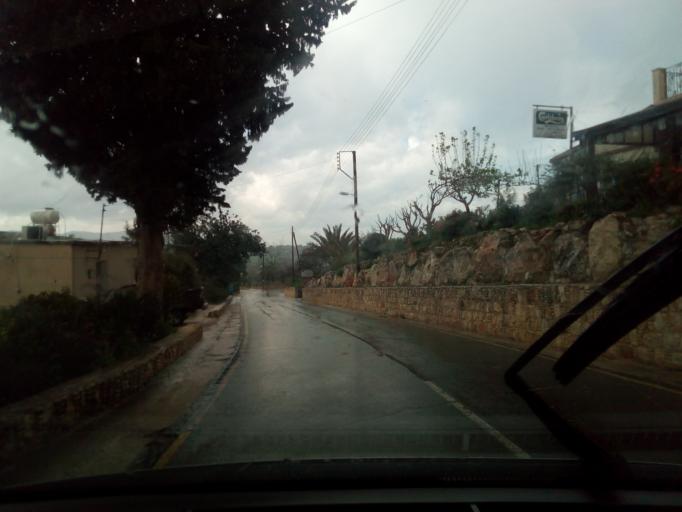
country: CY
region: Pafos
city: Polis
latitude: 34.9998
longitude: 32.4704
